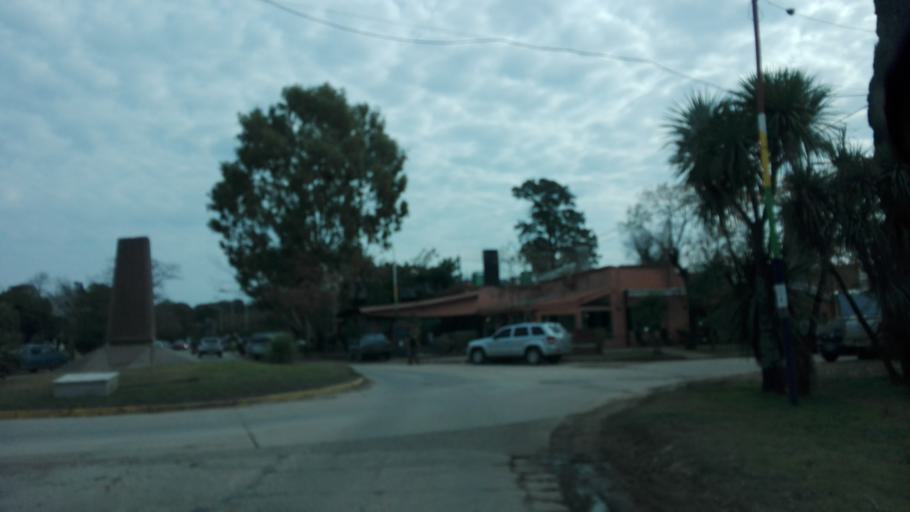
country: AR
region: Buenos Aires
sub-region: Partido de Chascomus
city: Chascomus
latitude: -35.5832
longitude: -58.0043
